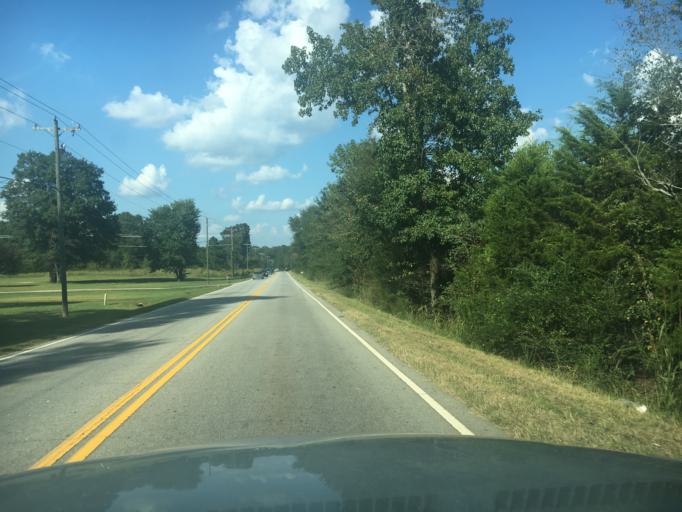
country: US
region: South Carolina
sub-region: Greenville County
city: Simpsonville
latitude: 34.6813
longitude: -82.2552
